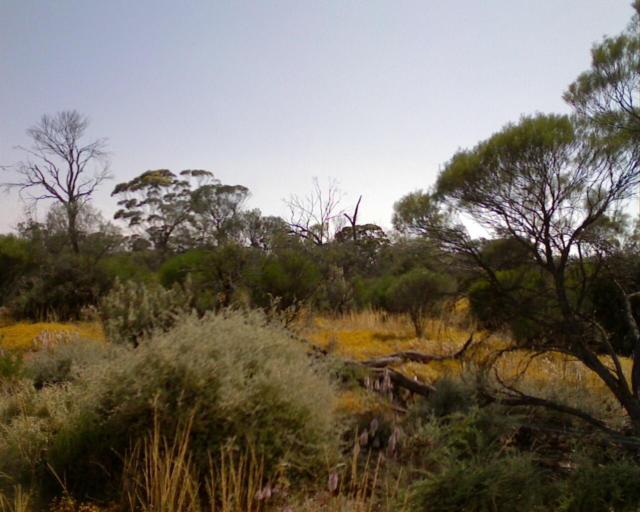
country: AU
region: Western Australia
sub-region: Merredin
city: Merredin
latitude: -30.9607
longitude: 118.8835
